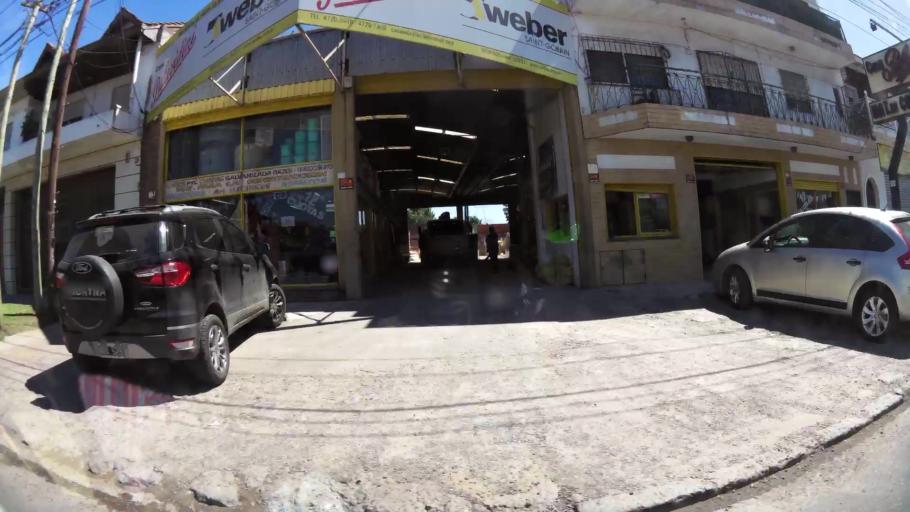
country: AR
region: Buenos Aires
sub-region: Partido de General San Martin
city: General San Martin
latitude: -34.5152
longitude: -58.5713
